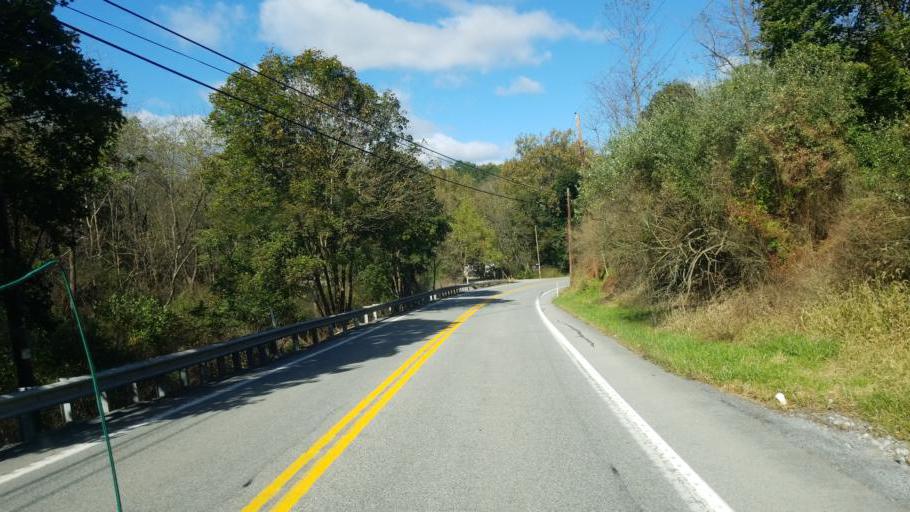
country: US
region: Pennsylvania
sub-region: Fulton County
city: McConnellsburg
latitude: 39.9783
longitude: -78.0427
